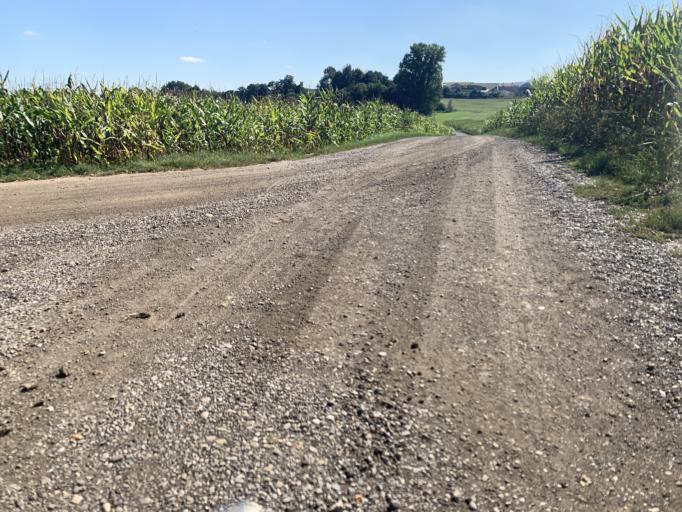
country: DE
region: Bavaria
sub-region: Swabia
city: Mering
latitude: 48.2905
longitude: 11.0129
